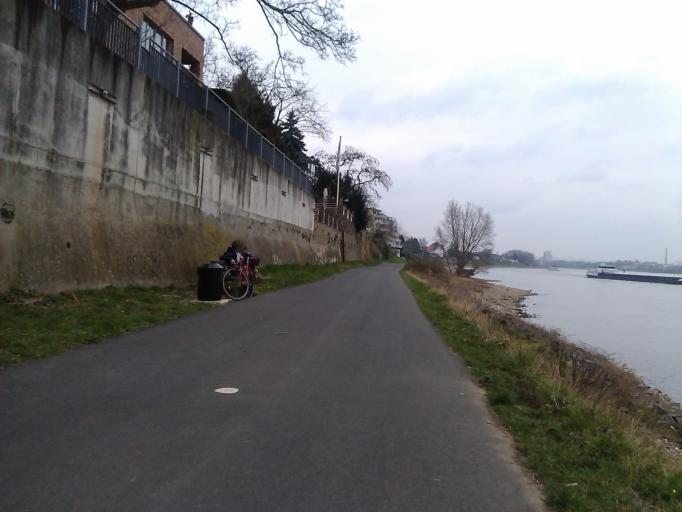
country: DE
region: North Rhine-Westphalia
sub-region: Regierungsbezirk Koln
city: Porz am Rhein
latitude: 50.8675
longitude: 7.0199
